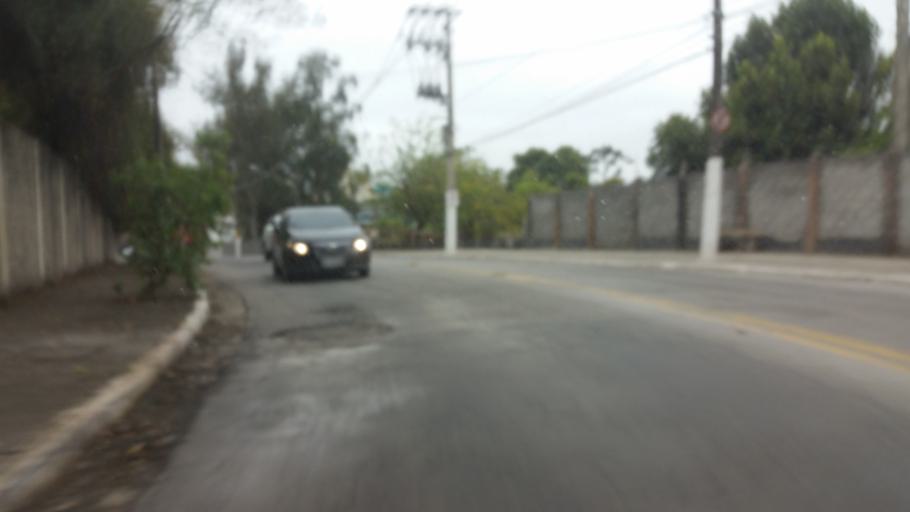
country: BR
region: Sao Paulo
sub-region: Diadema
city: Diadema
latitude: -23.6548
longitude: -46.6138
